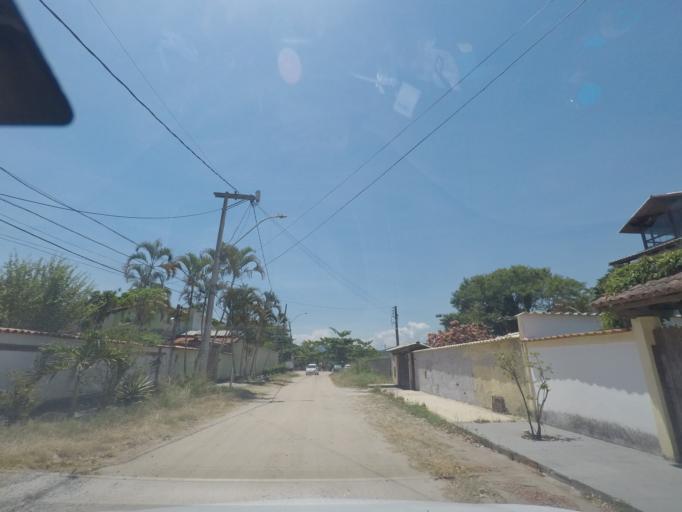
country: BR
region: Rio de Janeiro
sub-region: Niteroi
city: Niteroi
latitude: -22.9674
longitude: -43.0440
